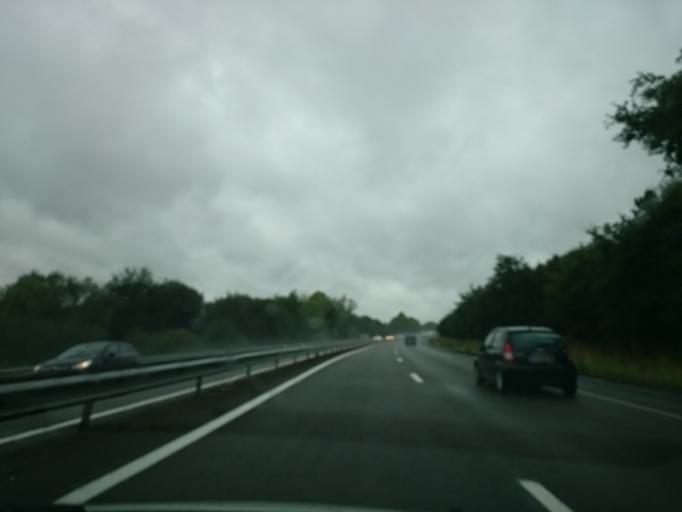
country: FR
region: Pays de la Loire
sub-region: Departement de la Loire-Atlantique
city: Orvault
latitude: 47.2815
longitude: -1.6035
